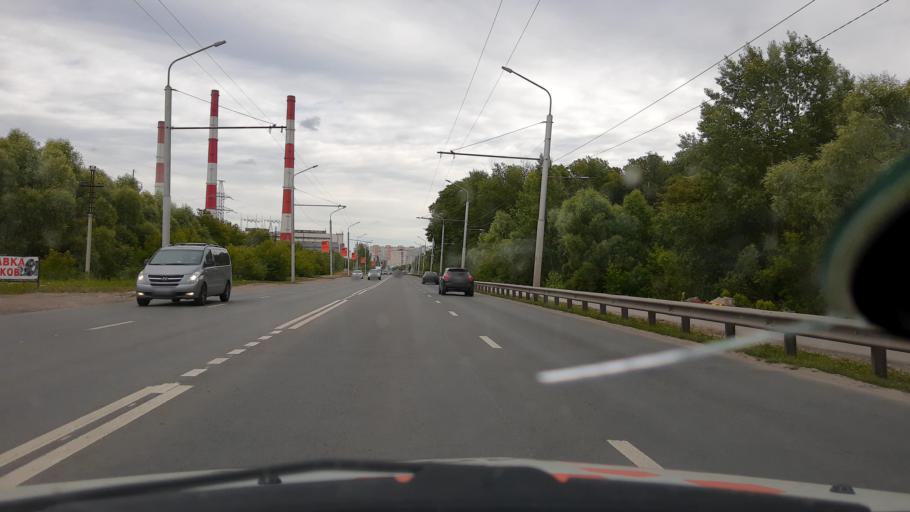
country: RU
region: Bashkortostan
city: Ufa
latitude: 54.7902
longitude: 56.1076
